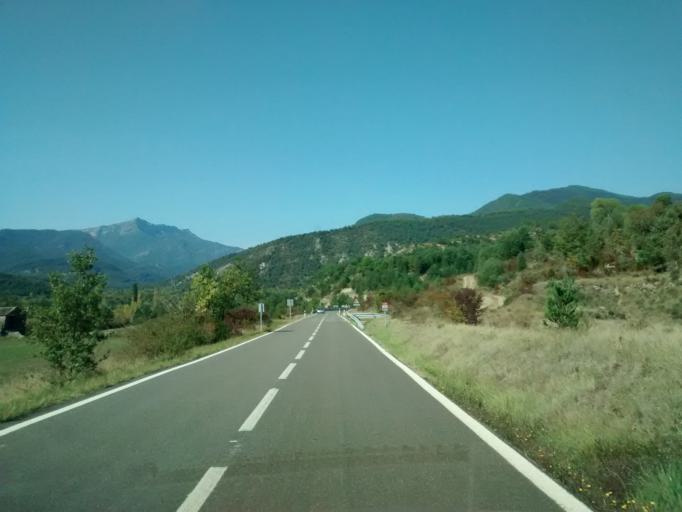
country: ES
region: Aragon
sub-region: Provincia de Huesca
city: Boltana
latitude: 42.4745
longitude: -0.0098
